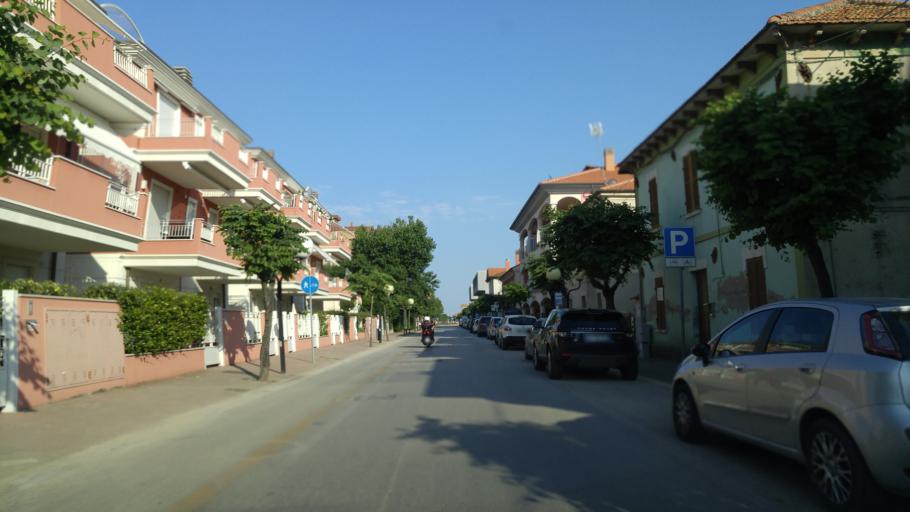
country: IT
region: The Marches
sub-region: Provincia di Pesaro e Urbino
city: Marotta
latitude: 43.7696
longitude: 13.1385
